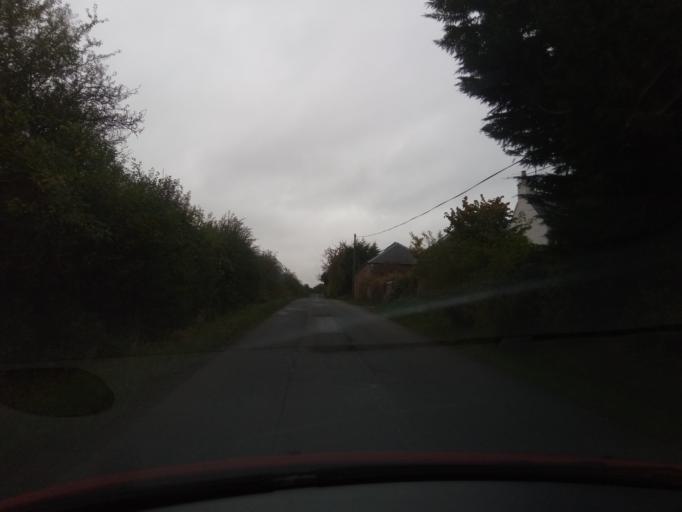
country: GB
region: Scotland
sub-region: The Scottish Borders
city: Saint Boswells
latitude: 55.5185
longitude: -2.6289
